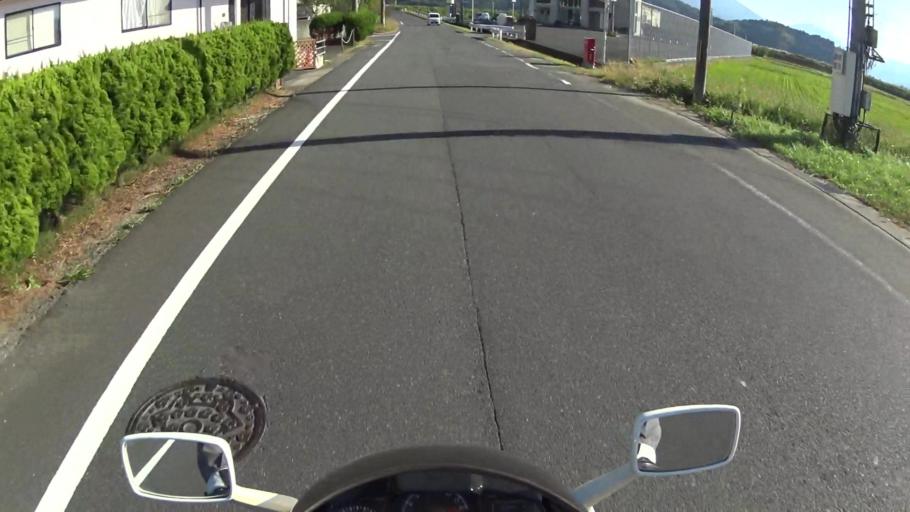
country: JP
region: Kyoto
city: Miyazu
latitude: 35.5349
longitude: 135.1147
